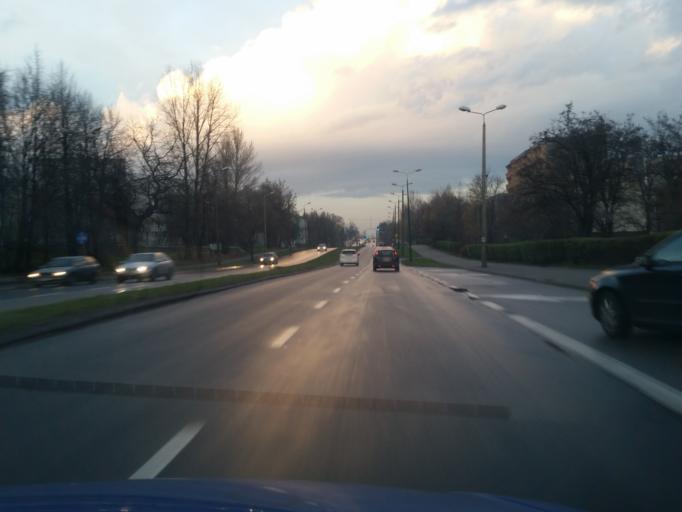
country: PL
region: Silesian Voivodeship
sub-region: Dabrowa Gornicza
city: Dabrowa Gornicza
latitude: 50.3070
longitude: 19.1906
